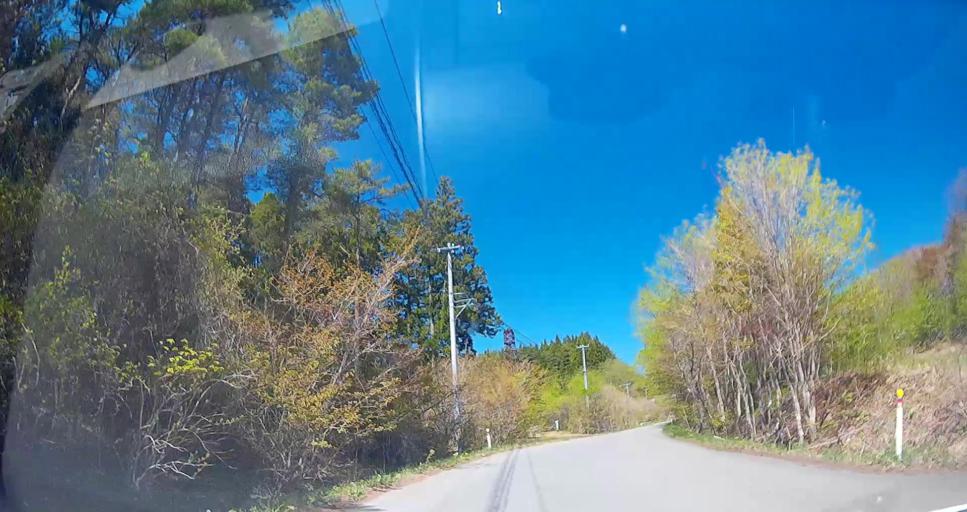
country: JP
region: Aomori
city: Mutsu
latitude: 41.2501
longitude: 141.3899
